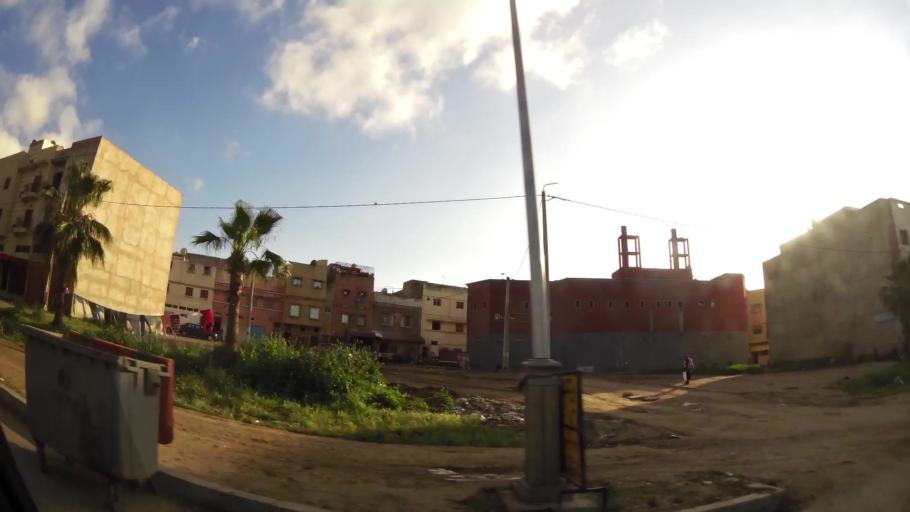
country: MA
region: Chaouia-Ouardigha
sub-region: Settat Province
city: Settat
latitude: 33.0039
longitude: -7.6082
